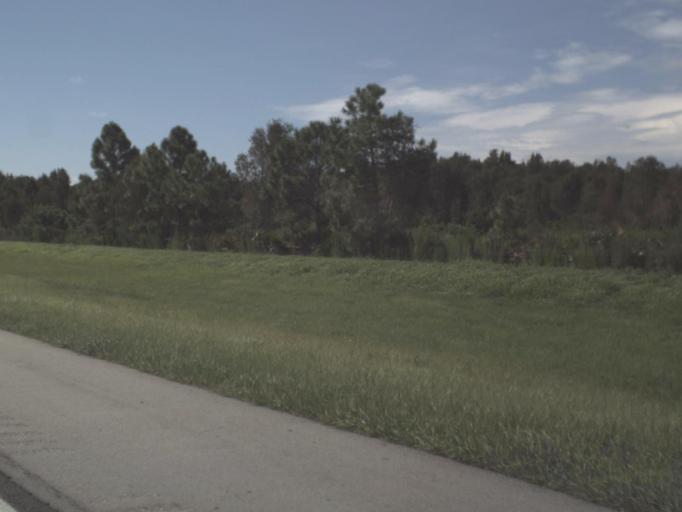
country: US
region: Florida
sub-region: Charlotte County
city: Charlotte Park
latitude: 26.8694
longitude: -81.9752
